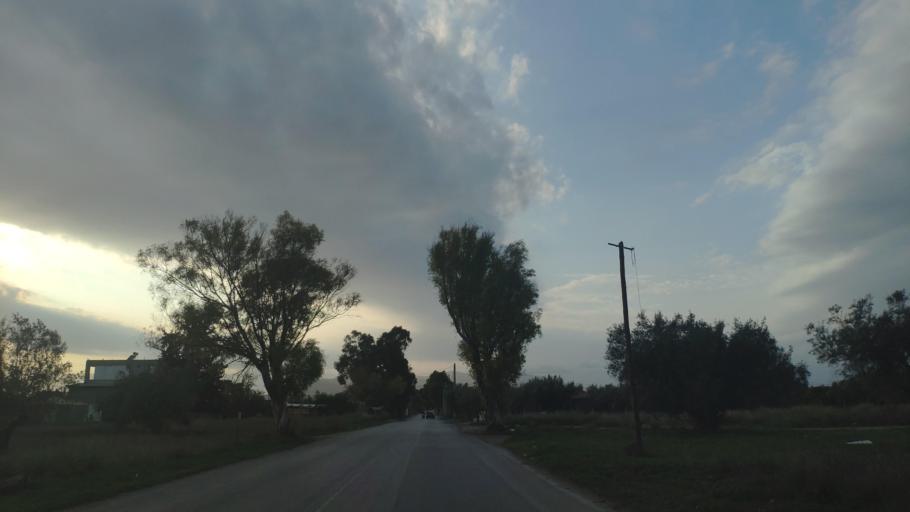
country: GR
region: Attica
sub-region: Nomarchia Dytikis Attikis
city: Nea Peramos
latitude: 37.9998
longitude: 23.3850
